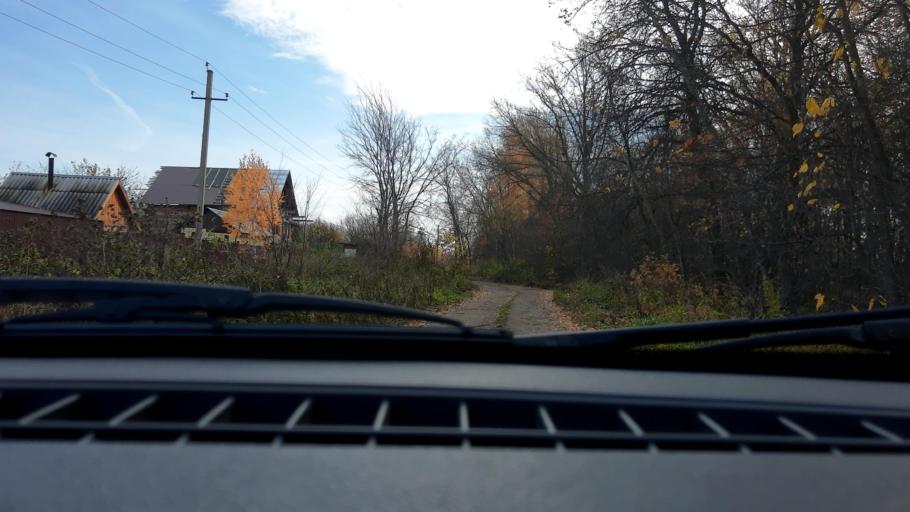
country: RU
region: Bashkortostan
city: Mikhaylovka
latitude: 54.8085
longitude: 55.8323
